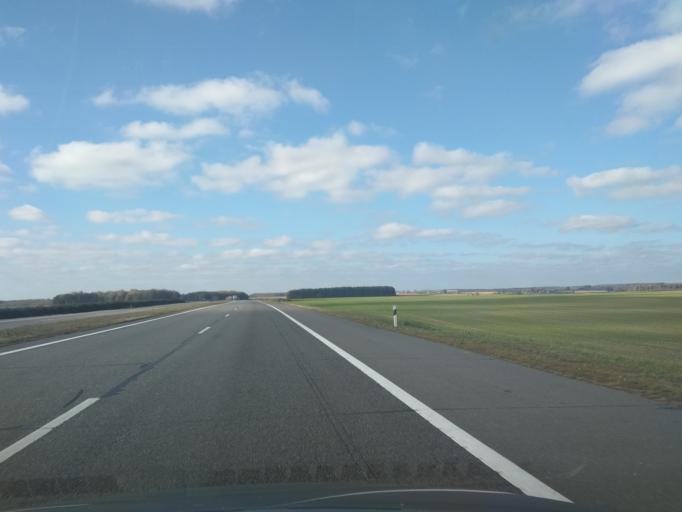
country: BY
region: Minsk
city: Stowbtsy
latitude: 53.5367
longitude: 26.7978
